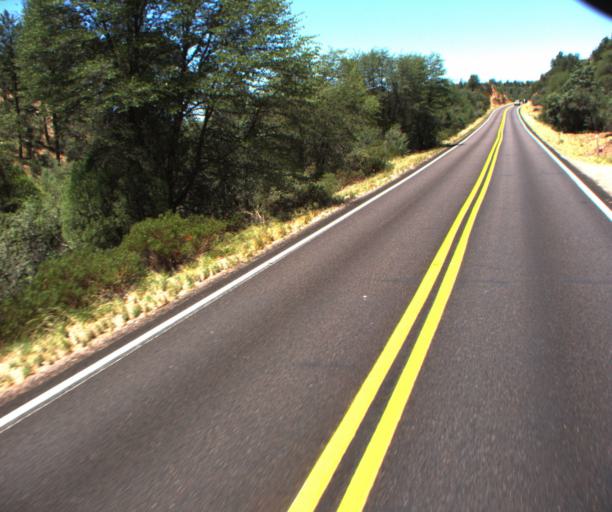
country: US
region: Arizona
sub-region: Gila County
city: Payson
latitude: 34.2852
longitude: -111.3359
